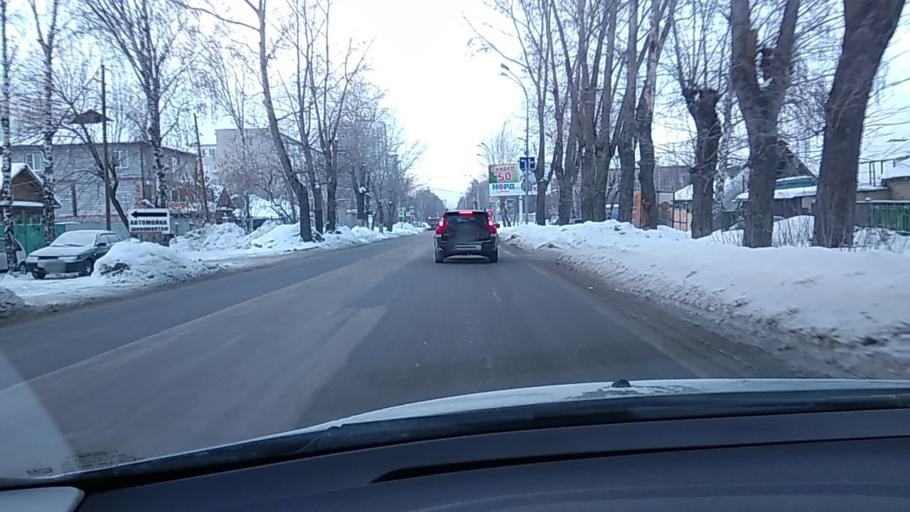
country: RU
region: Sverdlovsk
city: Yekaterinburg
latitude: 56.8107
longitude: 60.5807
